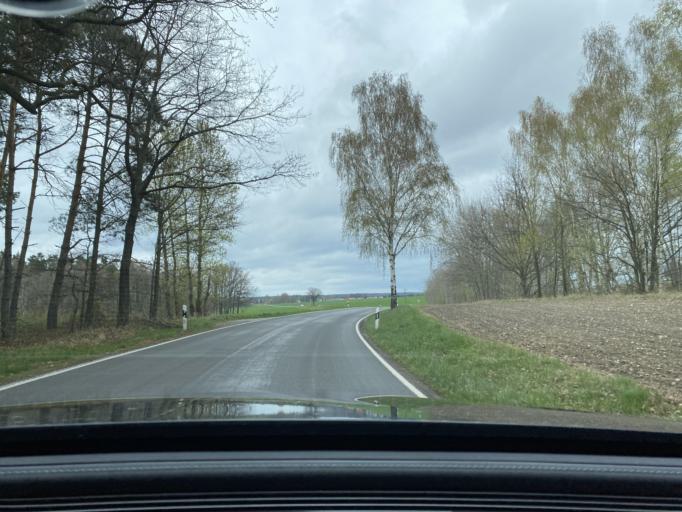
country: DE
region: Saxony
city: Puschwitz
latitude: 51.2601
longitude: 14.3067
